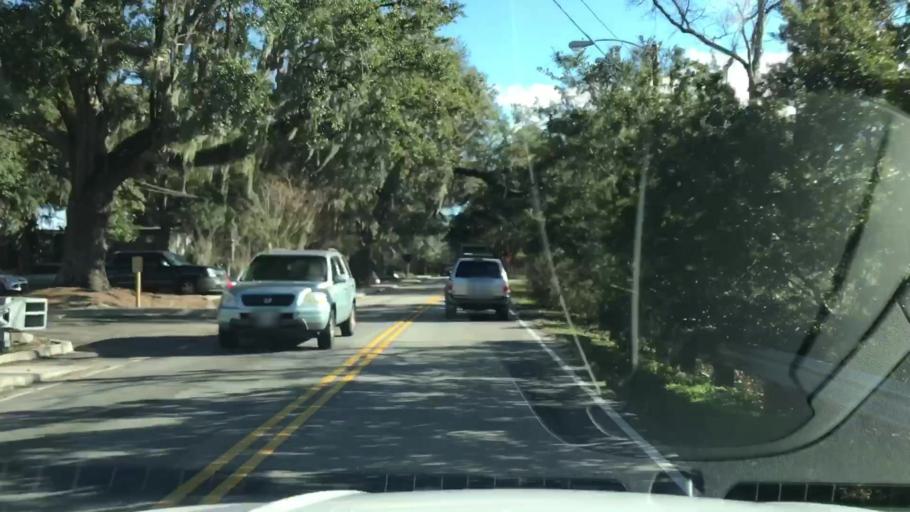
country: US
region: South Carolina
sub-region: Charleston County
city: North Charleston
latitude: 32.8189
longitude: -80.0343
